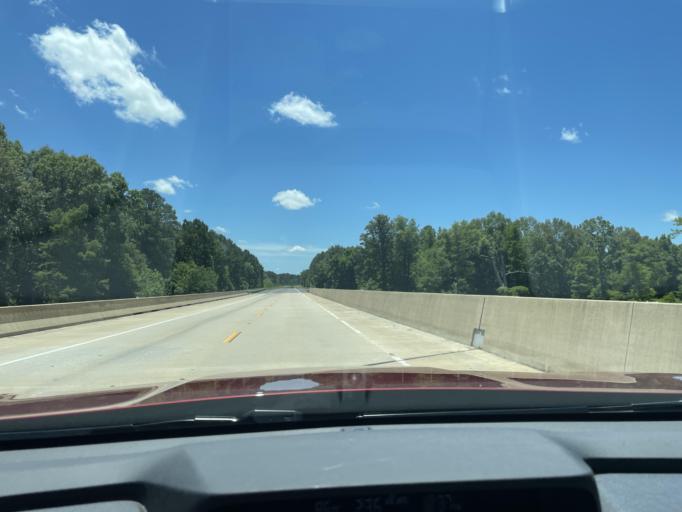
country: US
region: Arkansas
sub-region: Jefferson County
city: Pine Bluff
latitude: 34.1406
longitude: -91.9748
